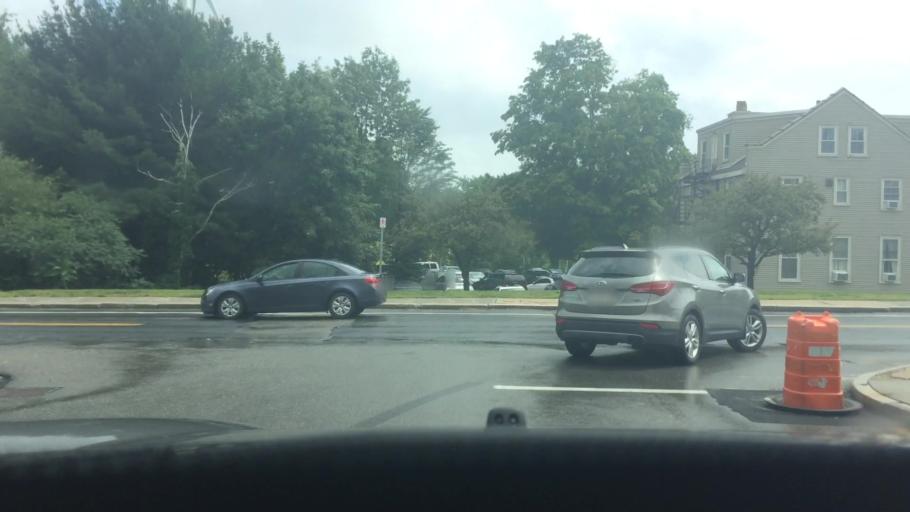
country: US
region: Massachusetts
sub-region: Worcester County
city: Gardner
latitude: 42.5873
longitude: -71.9868
